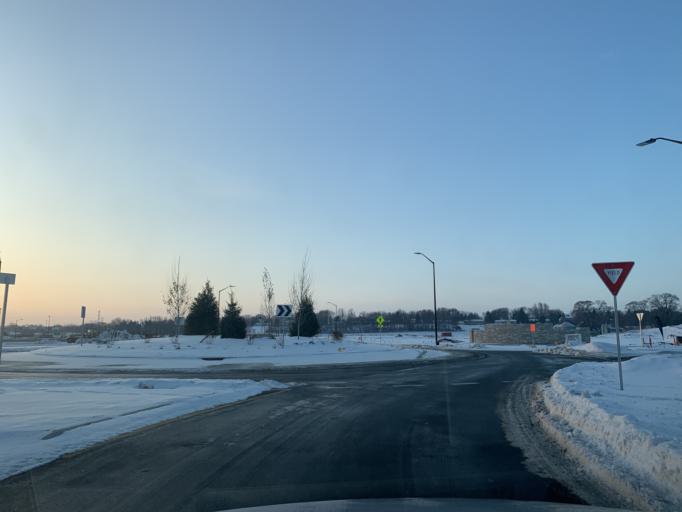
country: US
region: Minnesota
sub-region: Scott County
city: Shakopee
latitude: 44.7902
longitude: -93.4865
